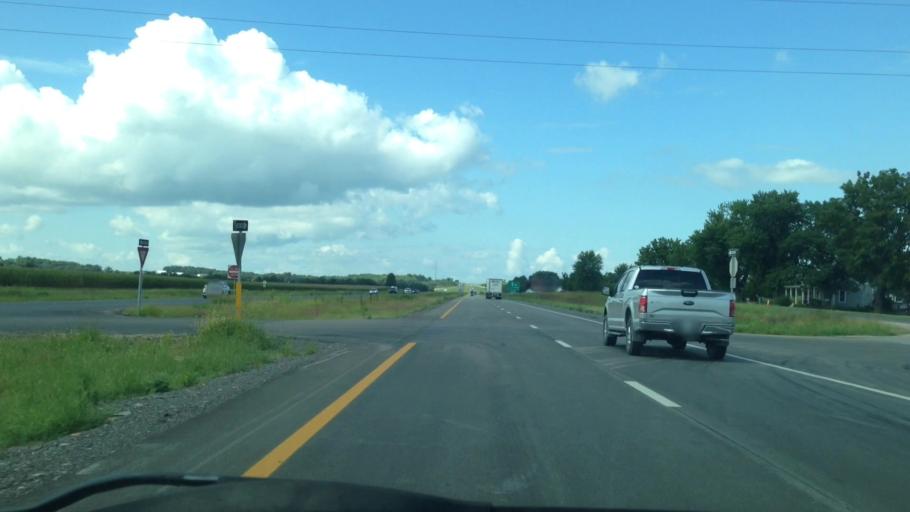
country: US
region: Illinois
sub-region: Adams County
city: Quincy
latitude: 39.9899
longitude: -91.5268
